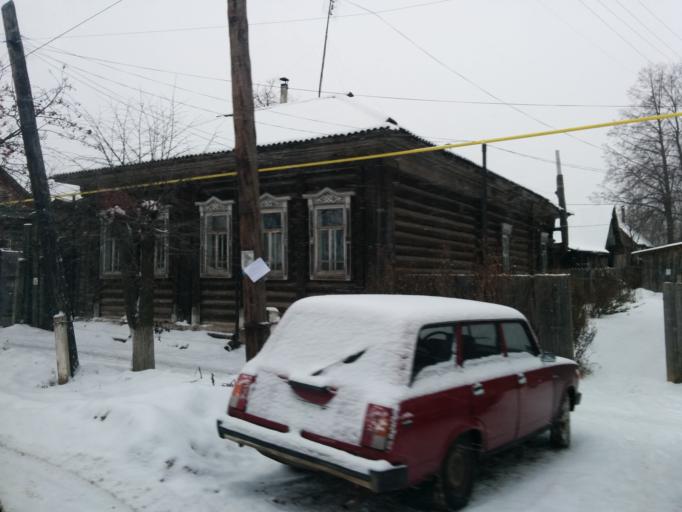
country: RU
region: Perm
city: Okhansk
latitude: 57.7255
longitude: 55.3879
